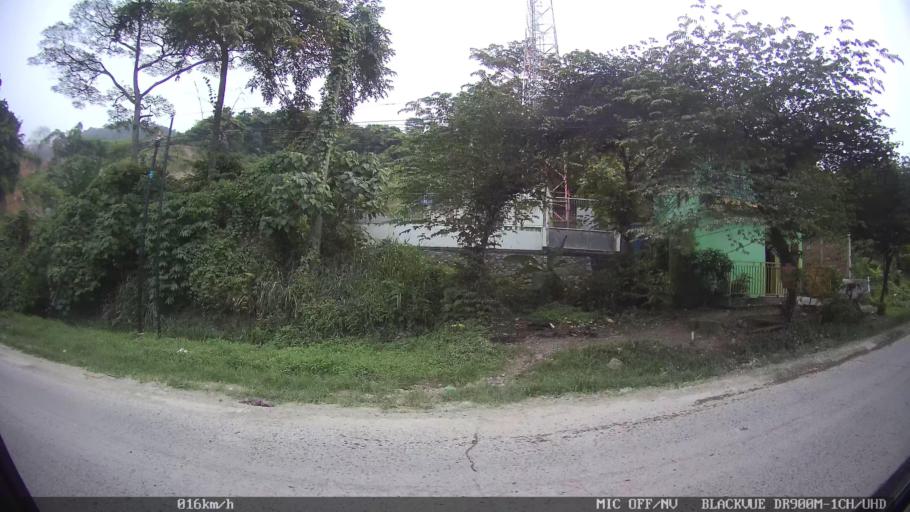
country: ID
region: Lampung
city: Panjang
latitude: -5.4414
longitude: 105.3113
